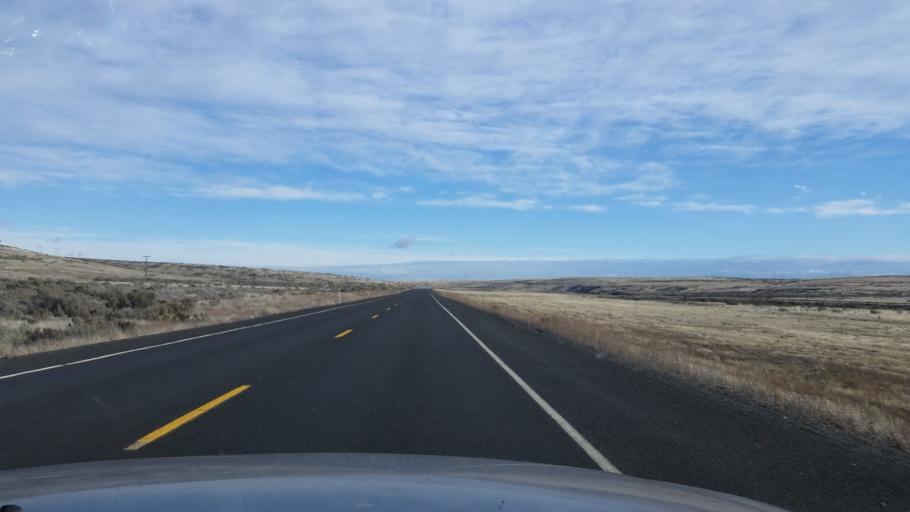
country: US
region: Washington
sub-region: Adams County
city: Ritzville
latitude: 47.3477
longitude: -118.5849
